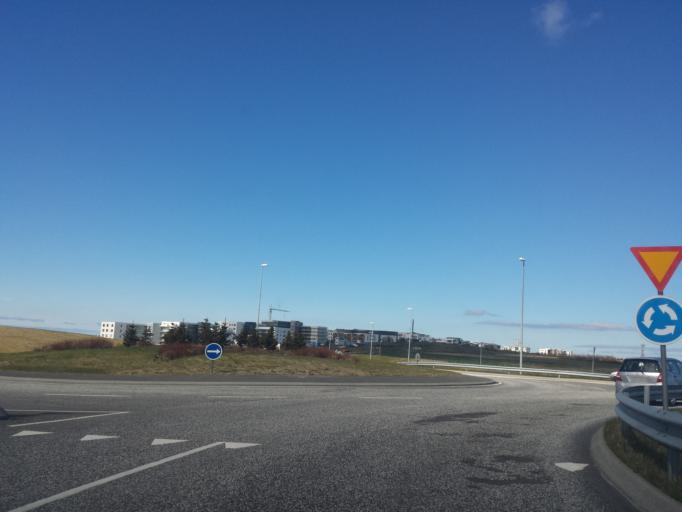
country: IS
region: Capital Region
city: Reykjavik
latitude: 64.0901
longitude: -21.8574
